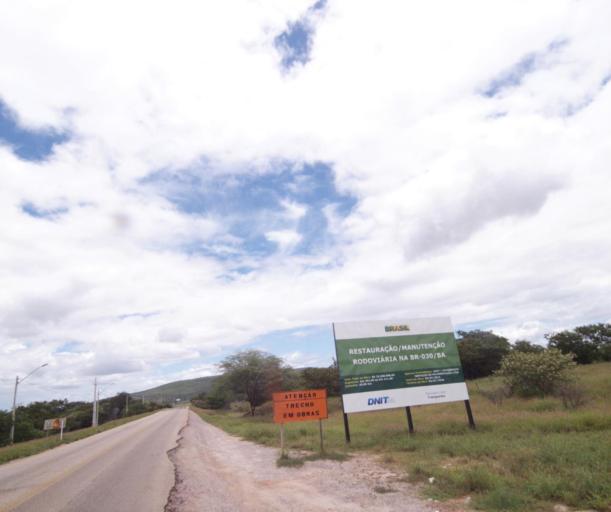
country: BR
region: Bahia
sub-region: Brumado
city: Brumado
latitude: -14.2145
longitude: -41.6449
